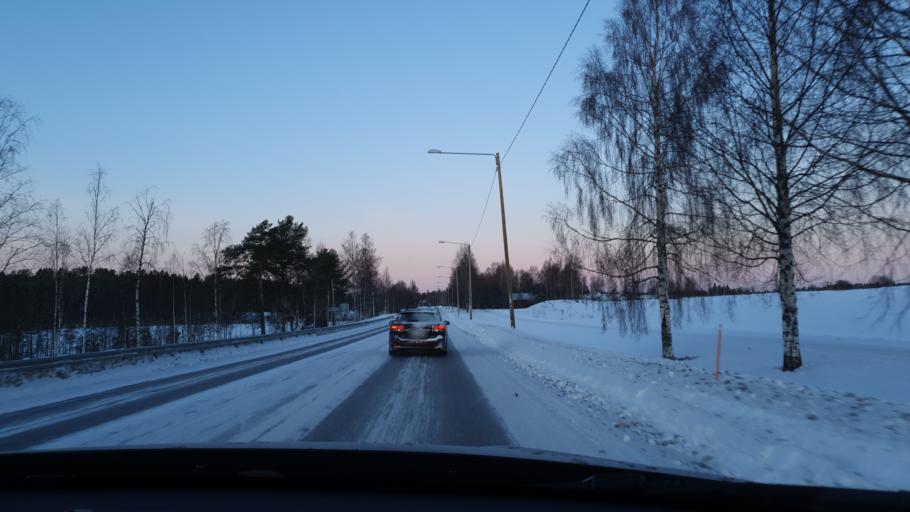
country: FI
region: Kainuu
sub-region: Kajaani
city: Sotkamo
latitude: 64.1250
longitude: 28.4225
